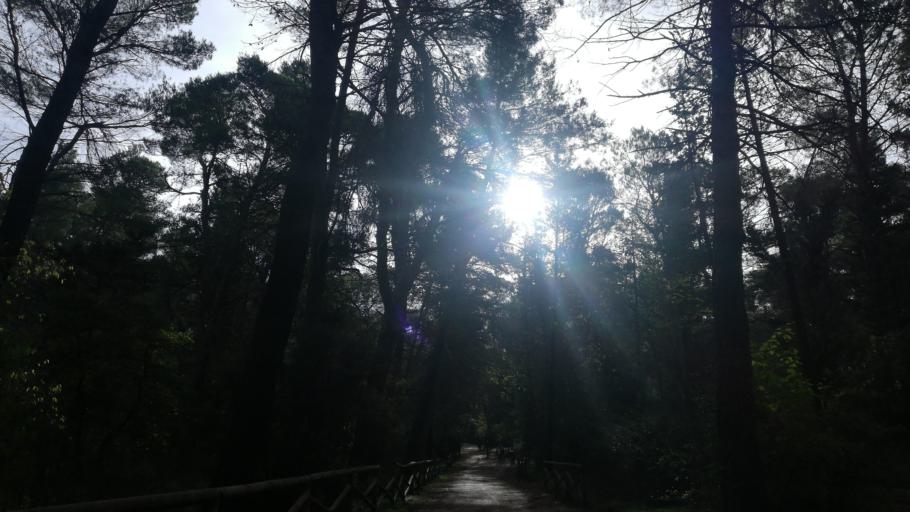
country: IT
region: Apulia
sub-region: Provincia di Bari
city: Cassano delle Murge
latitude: 40.8853
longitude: 16.7025
